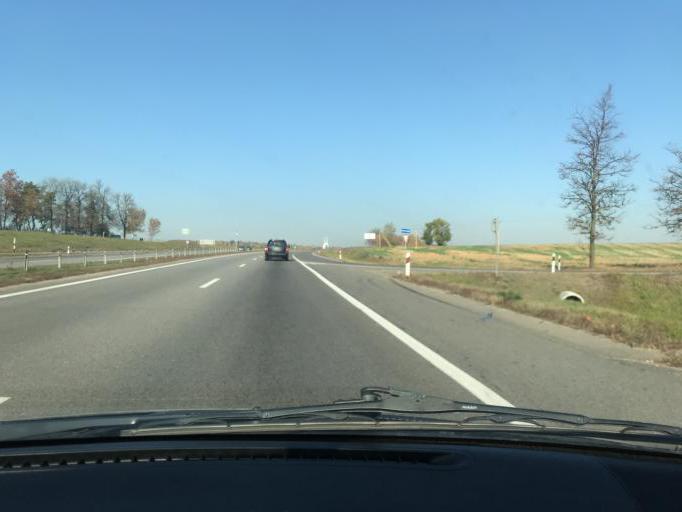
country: BY
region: Minsk
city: Samakhvalavichy
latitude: 53.7484
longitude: 27.5142
